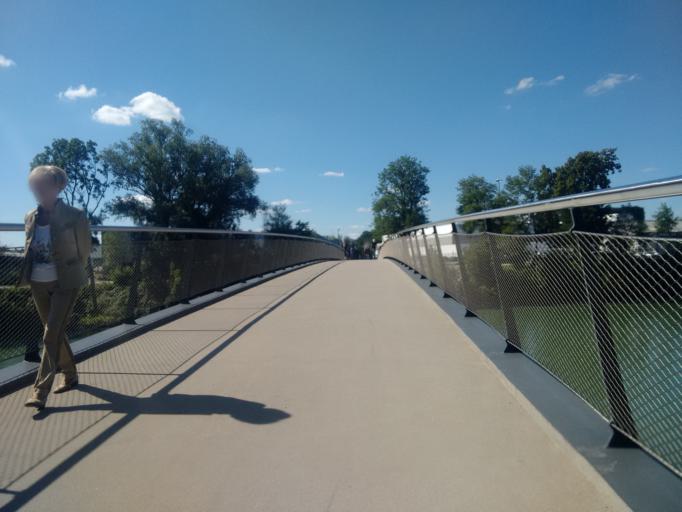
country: AT
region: Upper Austria
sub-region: Wels-Land
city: Thalheim bei Wels
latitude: 48.1484
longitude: 14.0181
